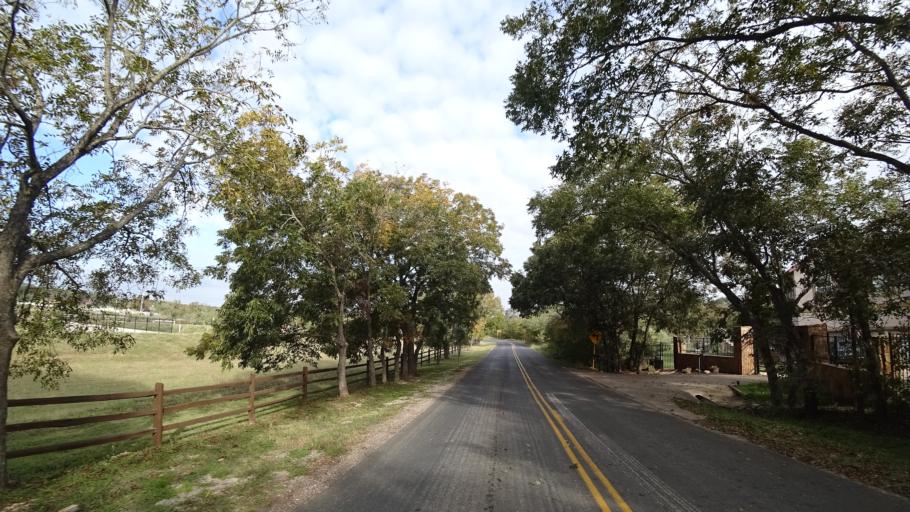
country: US
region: Texas
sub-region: Travis County
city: Manchaca
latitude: 30.1374
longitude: -97.8467
